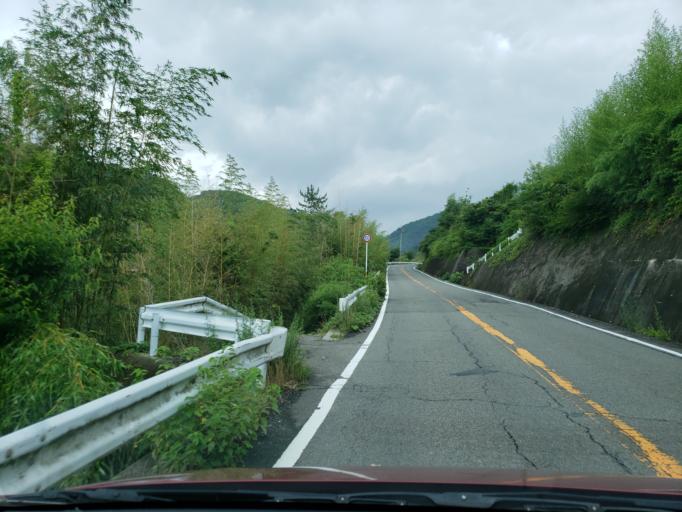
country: JP
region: Tokushima
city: Kamojimacho-jogejima
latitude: 34.1065
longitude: 134.2789
